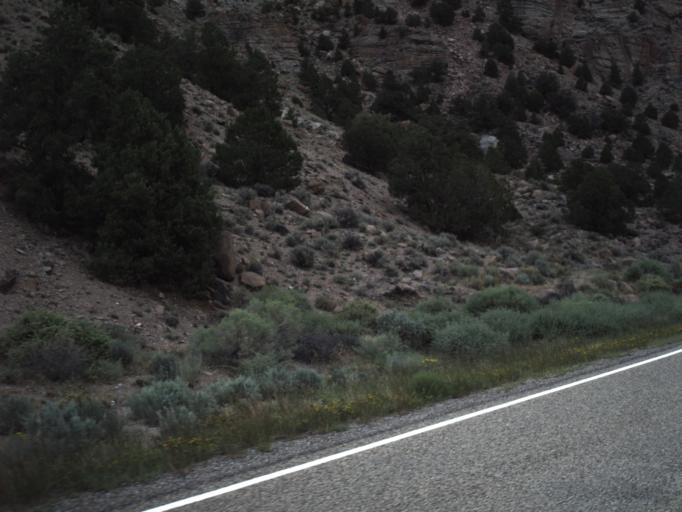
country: US
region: Utah
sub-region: Piute County
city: Junction
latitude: 38.1938
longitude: -112.1107
